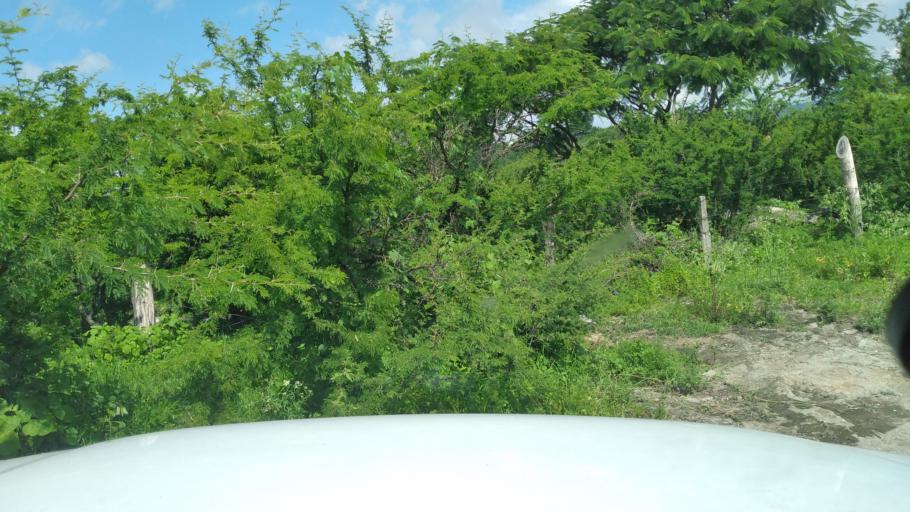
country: MX
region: Jalisco
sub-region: Zapopan
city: San Isidro
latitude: 20.7323
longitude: -103.2986
